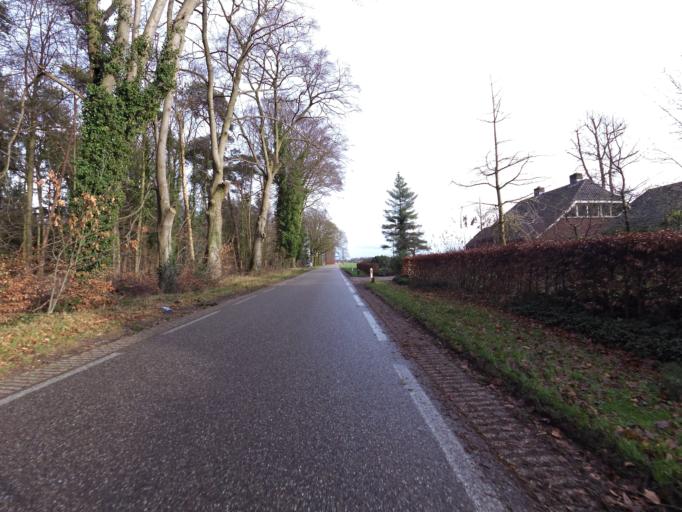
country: NL
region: Gelderland
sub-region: Gemeente Bronckhorst
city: Zelhem
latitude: 51.9674
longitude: 6.3775
